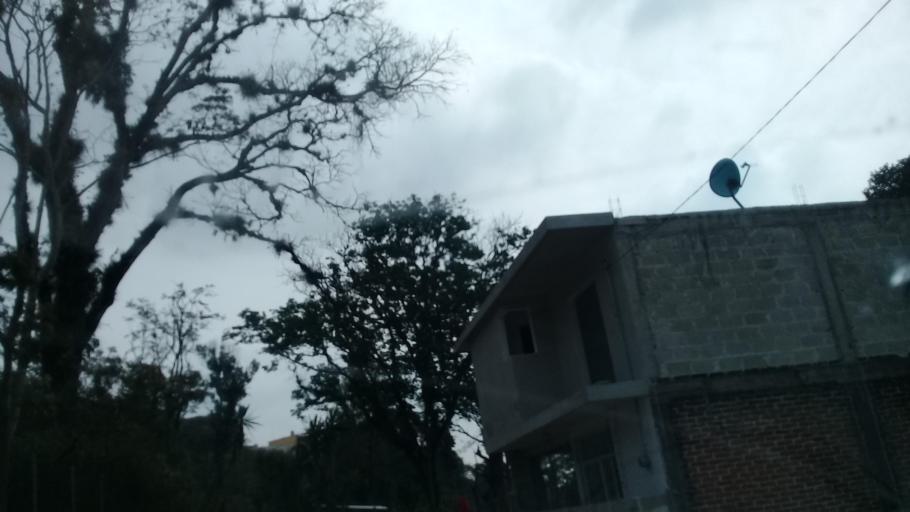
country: MX
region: Veracruz
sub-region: Xalapa
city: Fraccionamiento las Fuentes
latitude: 19.4957
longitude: -96.8985
